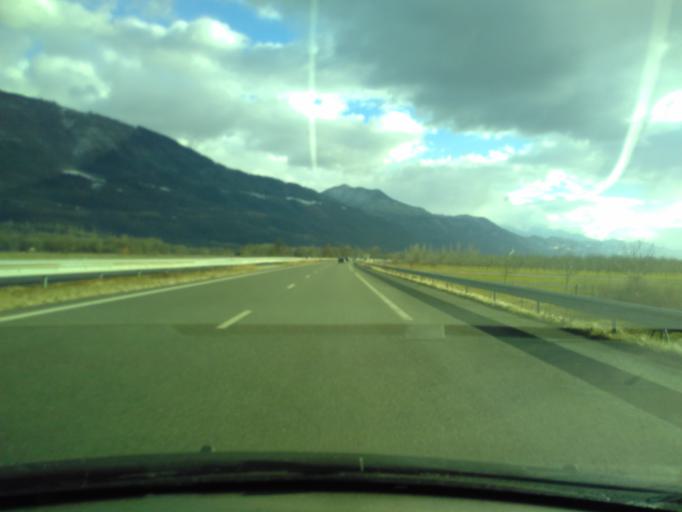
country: FR
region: Rhone-Alpes
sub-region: Departement de l'Isere
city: Pontcharra
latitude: 45.4174
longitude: 5.9986
